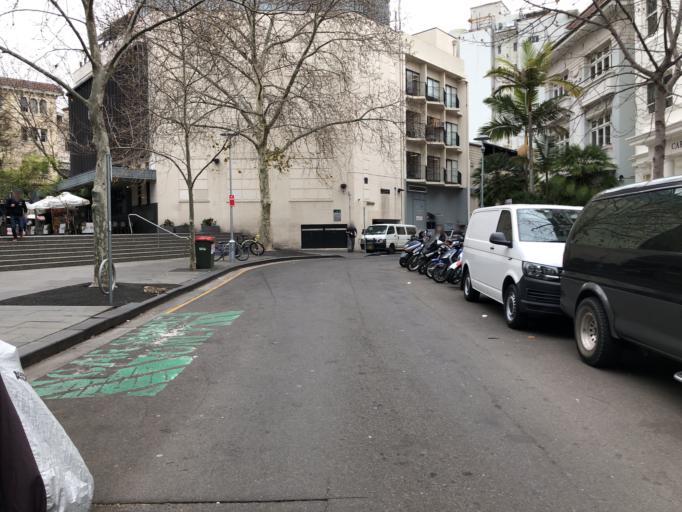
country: AU
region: New South Wales
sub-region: City of Sydney
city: Darlinghurst
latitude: -33.8729
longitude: 151.2237
